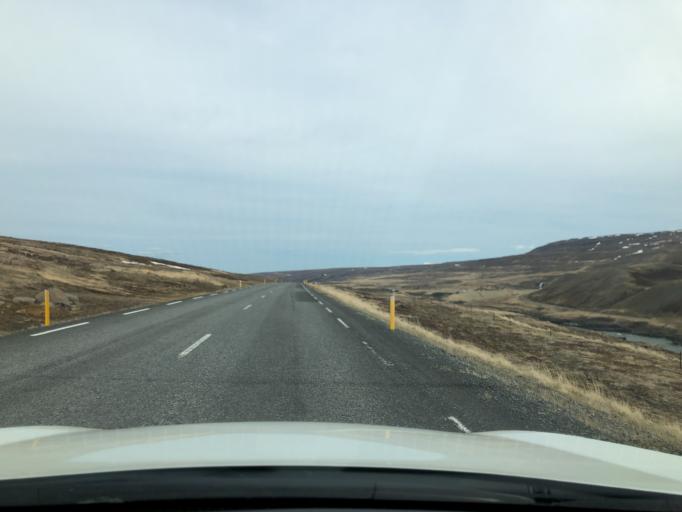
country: IS
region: East
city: Egilsstadir
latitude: 65.3920
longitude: -14.6853
